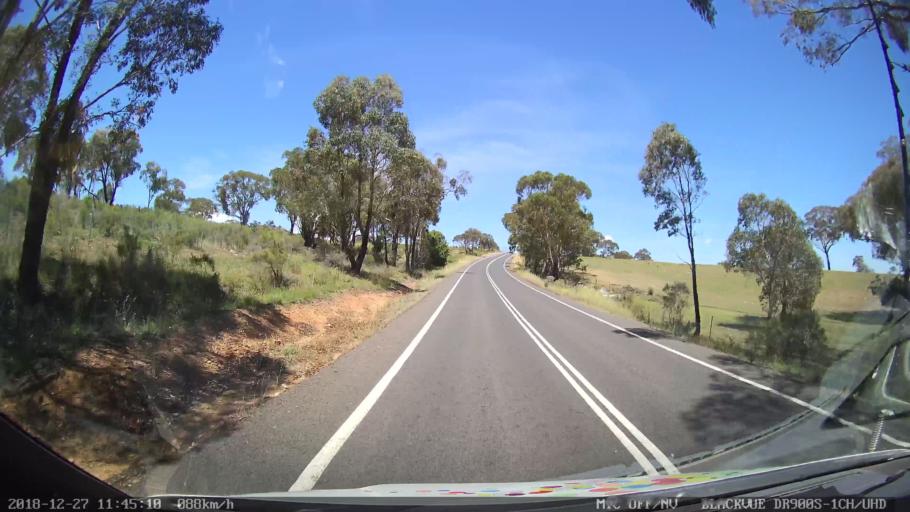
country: AU
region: New South Wales
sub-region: Bathurst Regional
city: Perthville
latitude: -33.5800
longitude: 149.4731
